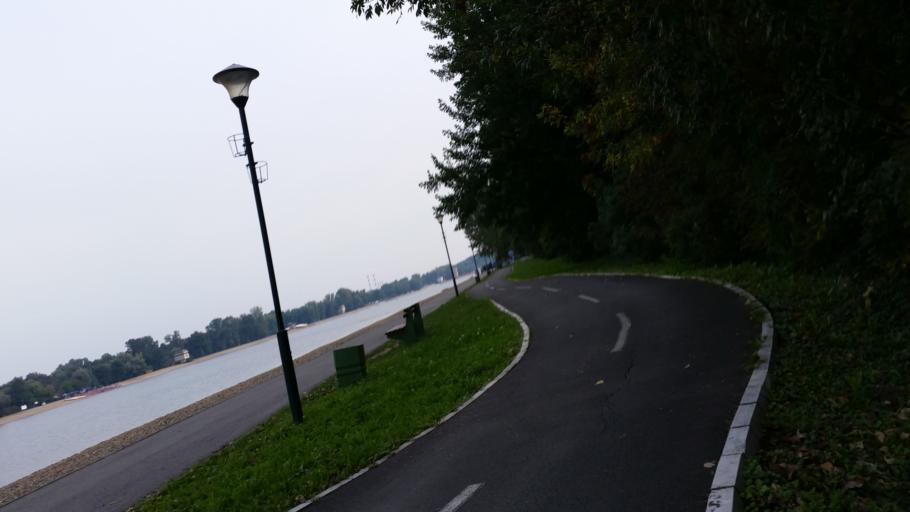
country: RS
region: Central Serbia
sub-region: Belgrade
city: Cukarica
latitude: 44.7780
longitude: 20.3786
